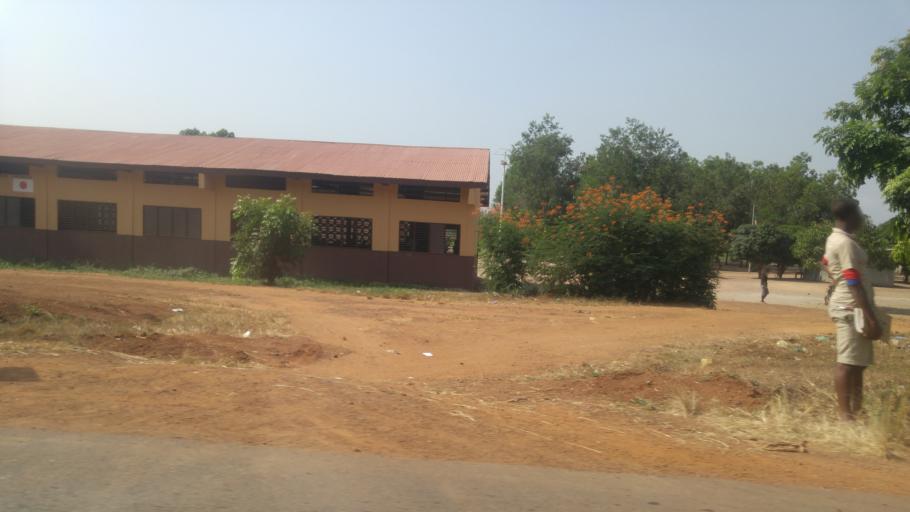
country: BJ
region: Zou
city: Bohicon
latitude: 7.0222
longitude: 2.1779
